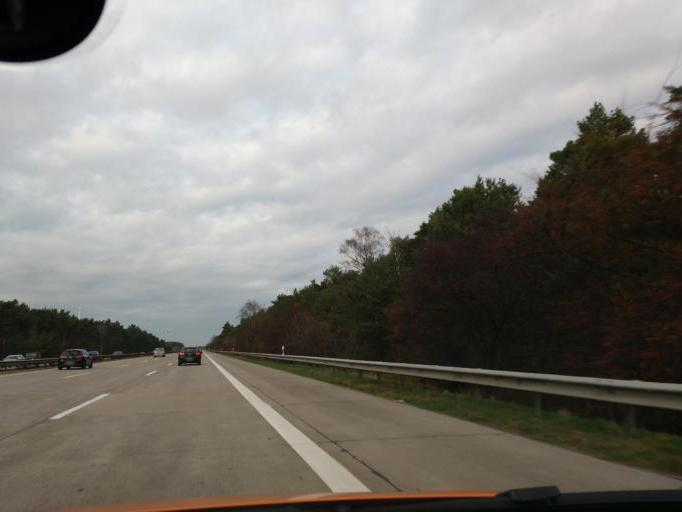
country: DE
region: Lower Saxony
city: Lindwedel
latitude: 52.6321
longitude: 9.7208
